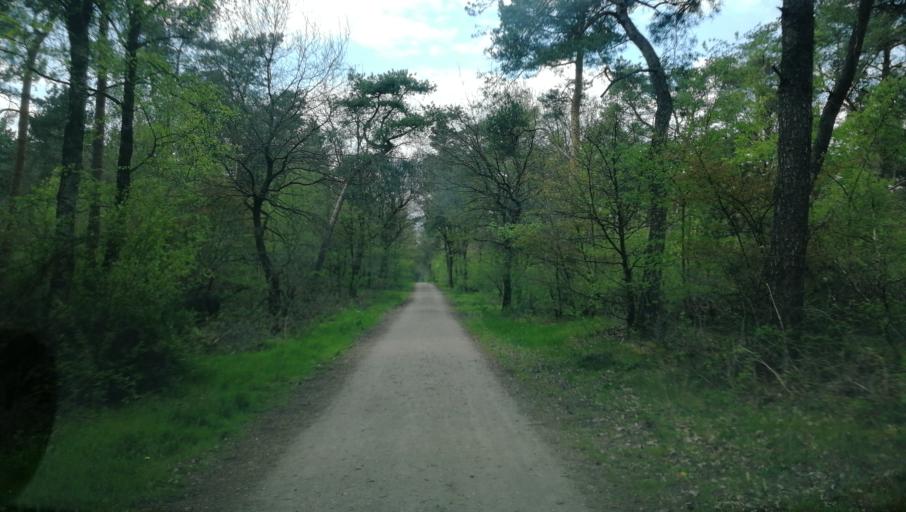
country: NL
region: Limburg
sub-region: Gemeente Peel en Maas
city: Maasbree
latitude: 51.3975
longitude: 5.9897
